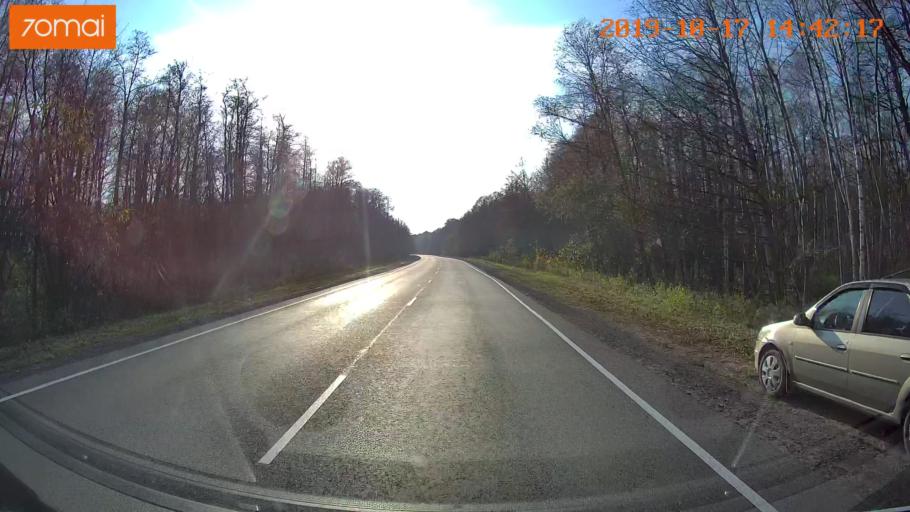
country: RU
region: Rjazan
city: Solotcha
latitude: 54.8387
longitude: 39.9271
